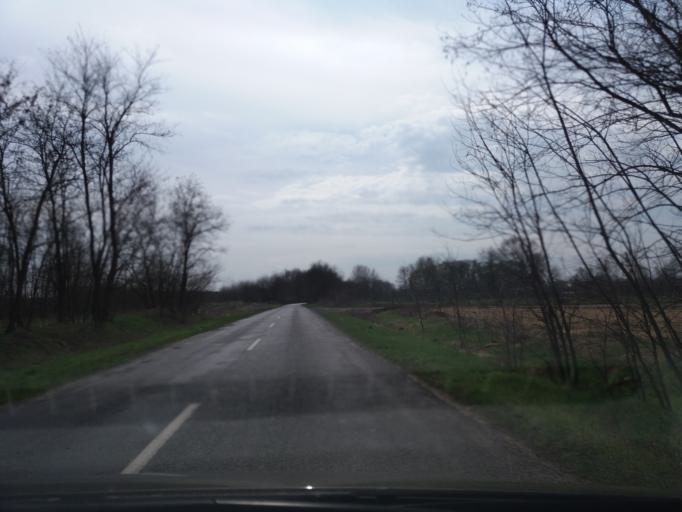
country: HU
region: Szabolcs-Szatmar-Bereg
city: Petnehaza
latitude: 48.0717
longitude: 22.0878
